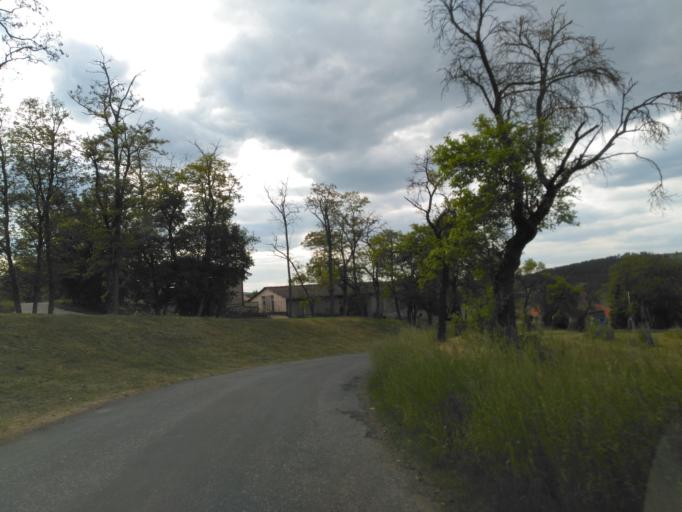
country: CZ
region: Central Bohemia
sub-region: Okres Beroun
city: Kraluv Dvur
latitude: 49.9195
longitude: 14.0668
